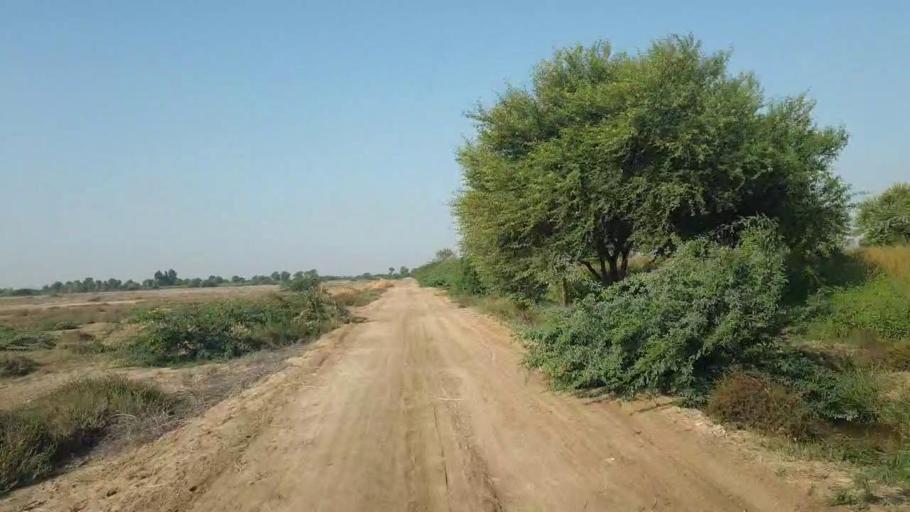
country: PK
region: Sindh
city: Badin
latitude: 24.4539
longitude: 68.7300
